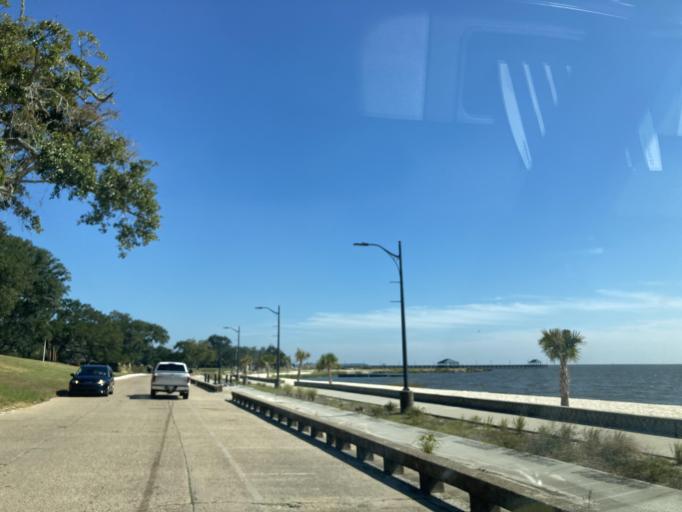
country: US
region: Mississippi
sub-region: Jackson County
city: Ocean Springs
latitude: 30.4071
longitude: -88.8328
